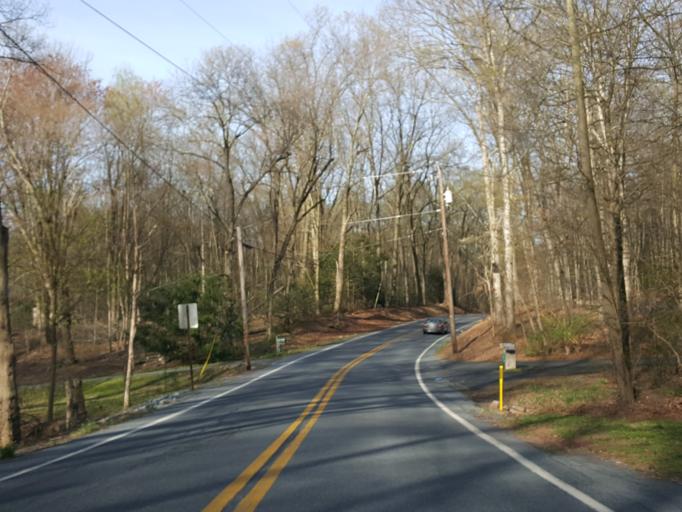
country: US
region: Pennsylvania
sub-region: Lebanon County
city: Annville
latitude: 40.2509
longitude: -76.4905
